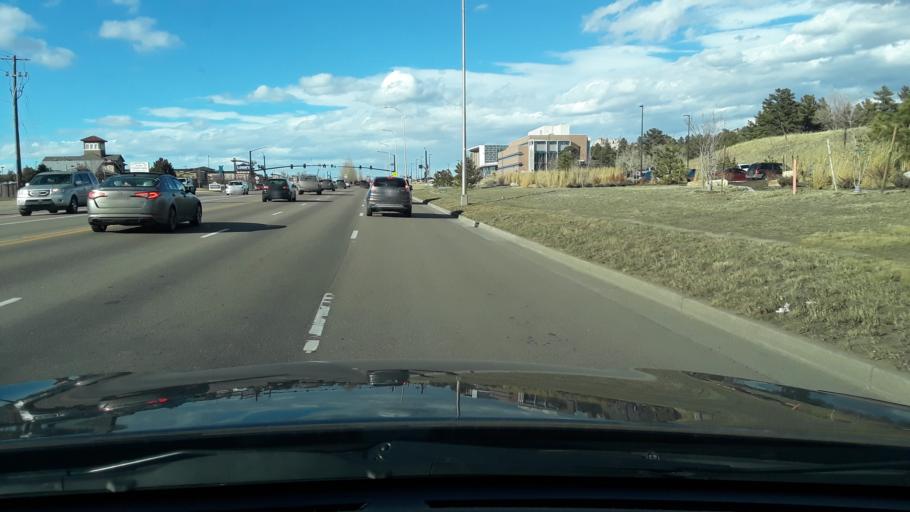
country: US
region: Colorado
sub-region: El Paso County
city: Colorado Springs
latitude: 38.8989
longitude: -104.8179
